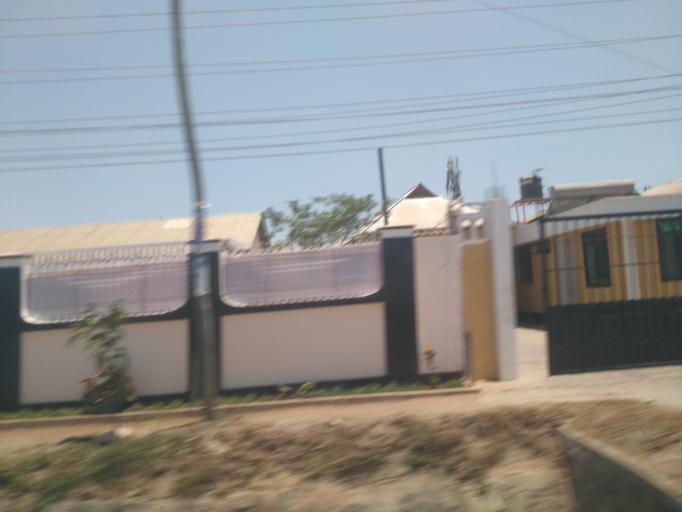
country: TZ
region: Dodoma
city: Dodoma
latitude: -6.1739
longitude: 35.7497
